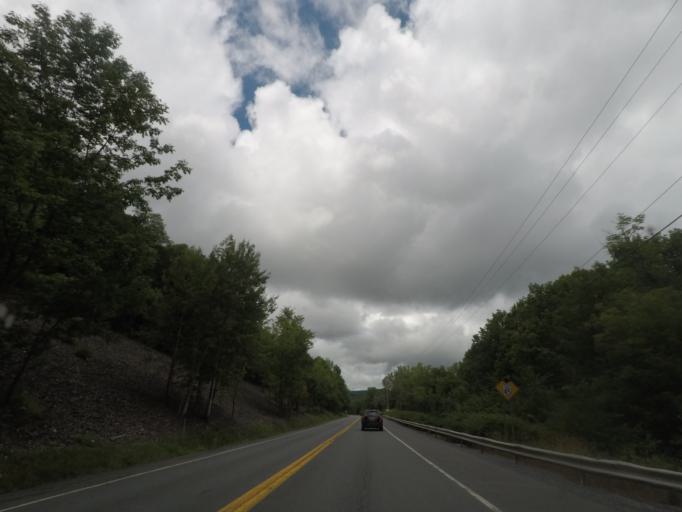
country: US
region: Massachusetts
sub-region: Berkshire County
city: Williamstown
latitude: 42.6874
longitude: -73.3685
